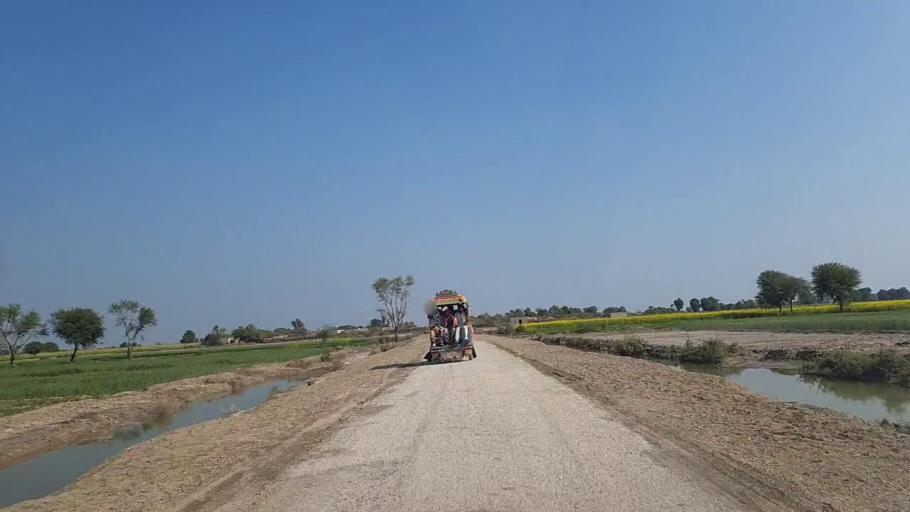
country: PK
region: Sindh
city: Jam Sahib
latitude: 26.2550
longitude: 68.5737
